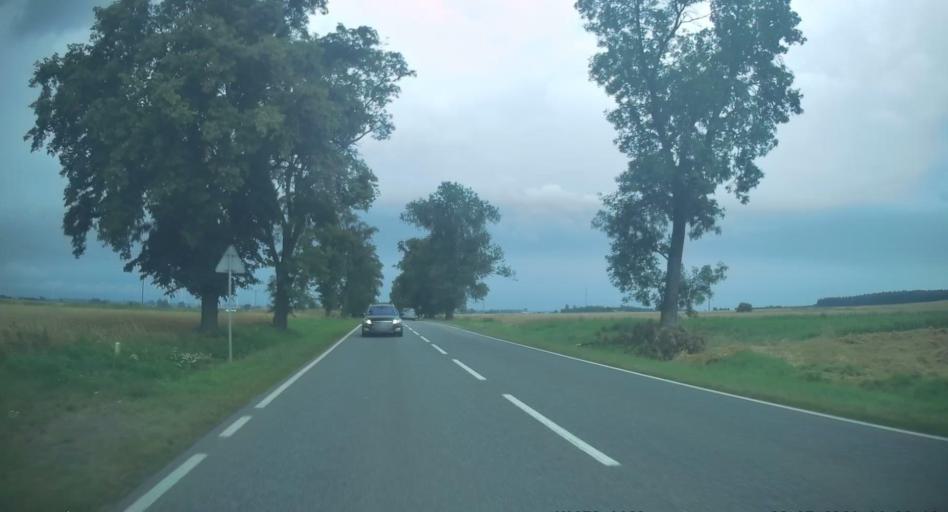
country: PL
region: Lodz Voivodeship
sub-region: Powiat skierniewicki
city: Gluchow
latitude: 51.7774
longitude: 20.1086
